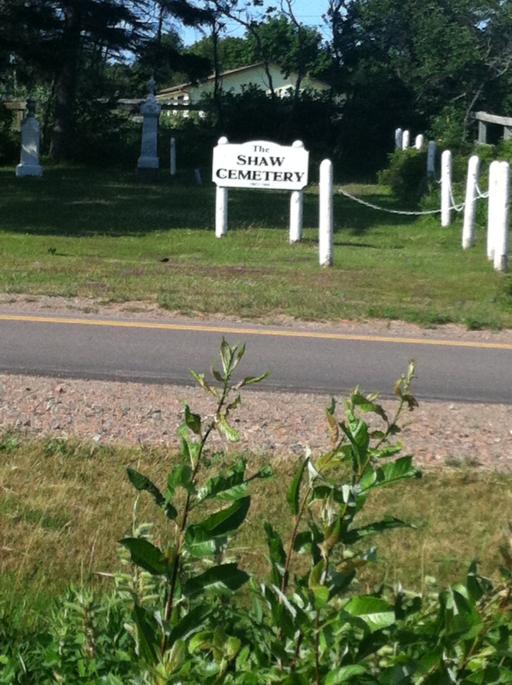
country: CA
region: Prince Edward Island
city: Charlottetown
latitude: 46.4144
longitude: -63.1150
